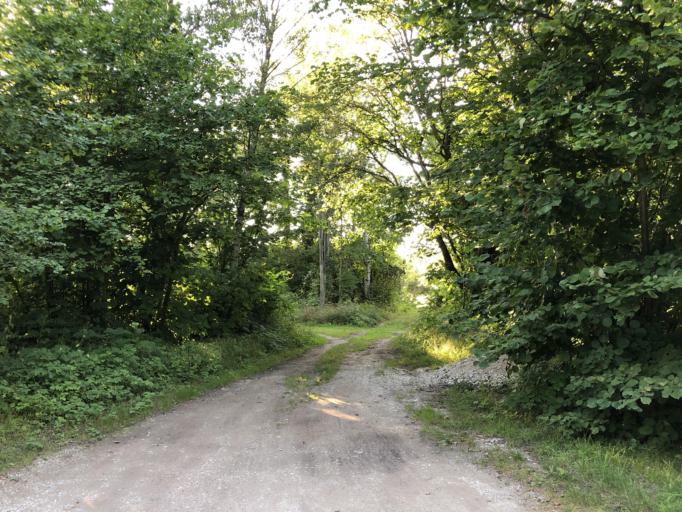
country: SE
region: Gotland
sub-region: Gotland
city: Hemse
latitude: 57.0331
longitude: 18.2718
